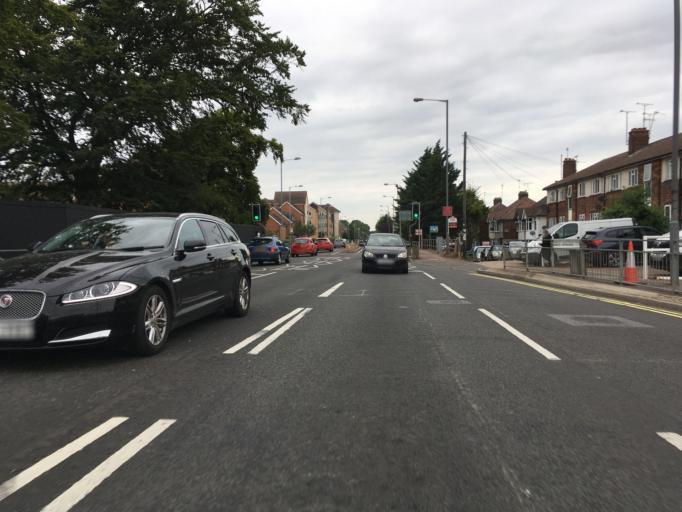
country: GB
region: England
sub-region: Central Bedfordshire
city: Dunstable
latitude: 51.8943
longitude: -0.5325
